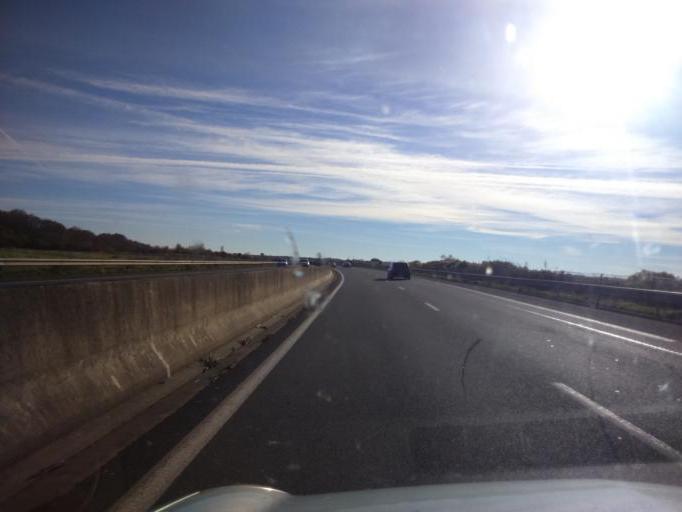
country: FR
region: Poitou-Charentes
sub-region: Departement de la Charente-Maritime
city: Saint-Laurent-de-la-Pree
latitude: 45.9817
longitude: -1.0159
